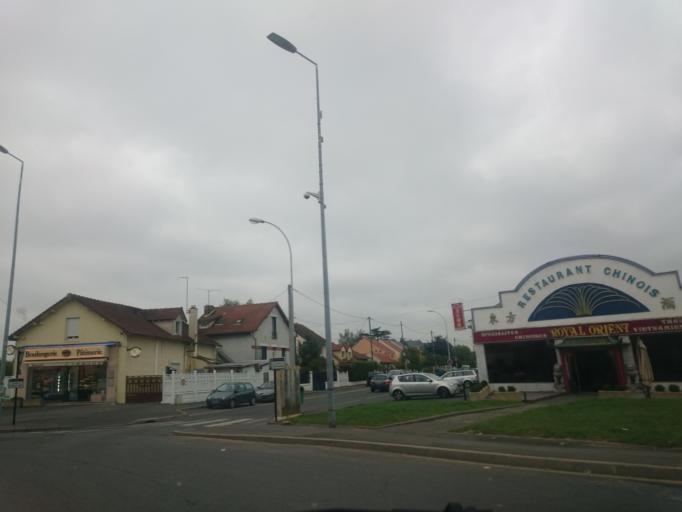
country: FR
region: Ile-de-France
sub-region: Departement de l'Essonne
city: Sainte-Genevieve-des-Bois
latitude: 48.6449
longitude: 2.3349
